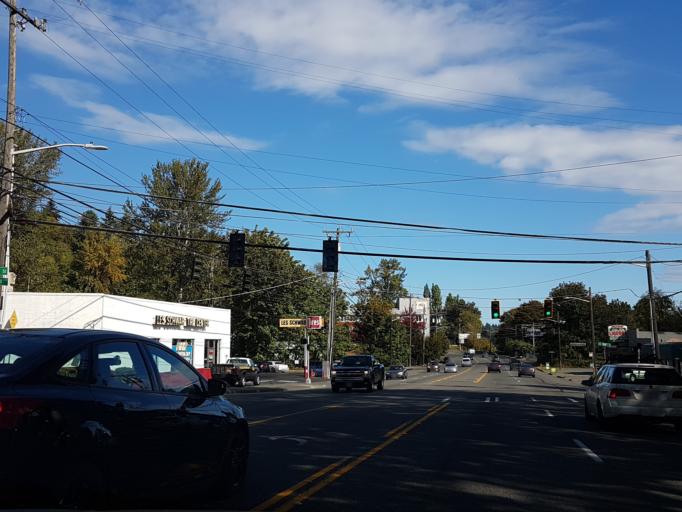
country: US
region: Washington
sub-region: King County
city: Lake Forest Park
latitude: 47.6999
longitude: -122.3035
